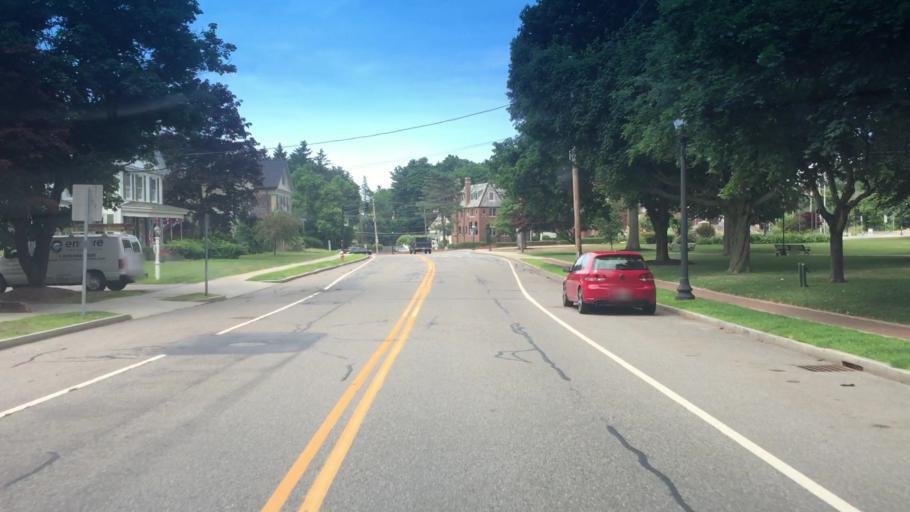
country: US
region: Massachusetts
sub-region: Norfolk County
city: Franklin
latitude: 42.0885
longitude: -71.4021
